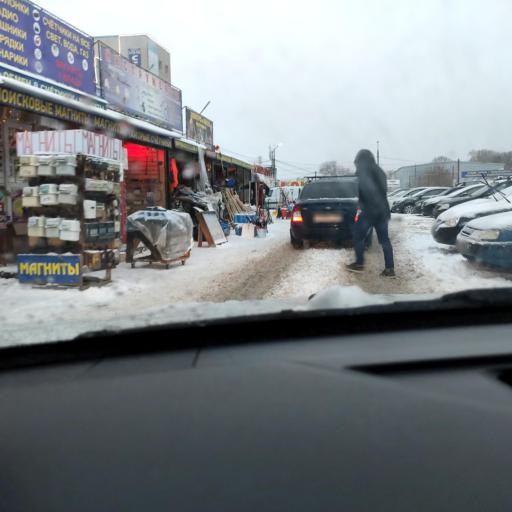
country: RU
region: Samara
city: Samara
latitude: 53.2090
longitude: 50.2520
